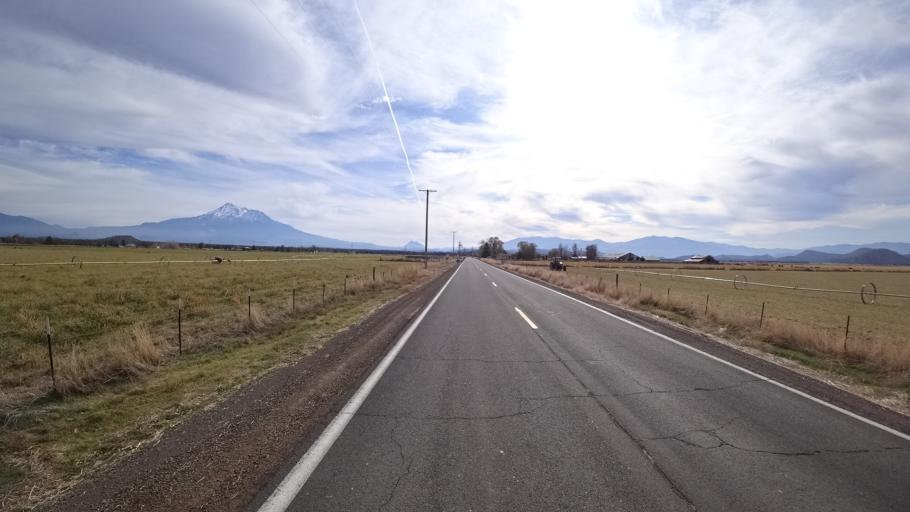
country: US
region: California
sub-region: Siskiyou County
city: Montague
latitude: 41.6211
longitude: -122.3996
